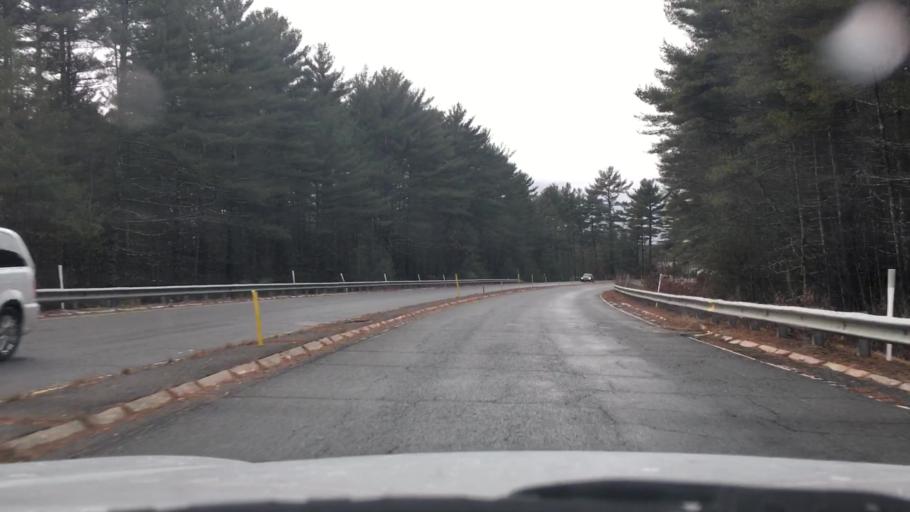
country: US
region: Massachusetts
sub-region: Franklin County
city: Orange
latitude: 42.5589
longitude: -72.2827
